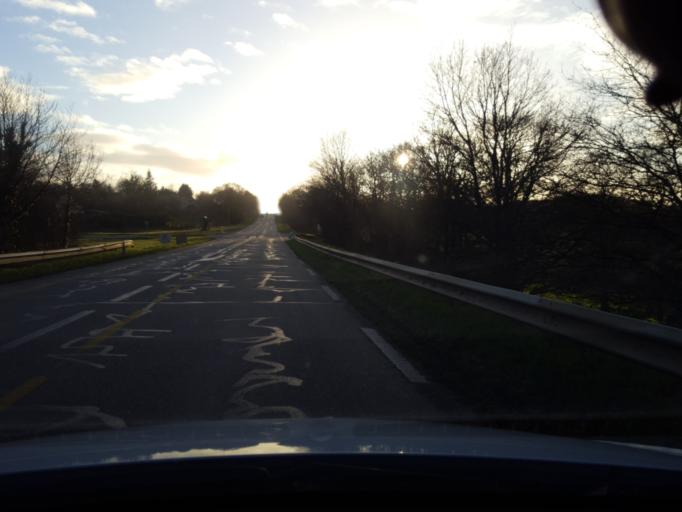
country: FR
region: Brittany
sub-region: Departement d'Ille-et-Vilaine
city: Guignen
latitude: 47.9374
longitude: -1.8422
